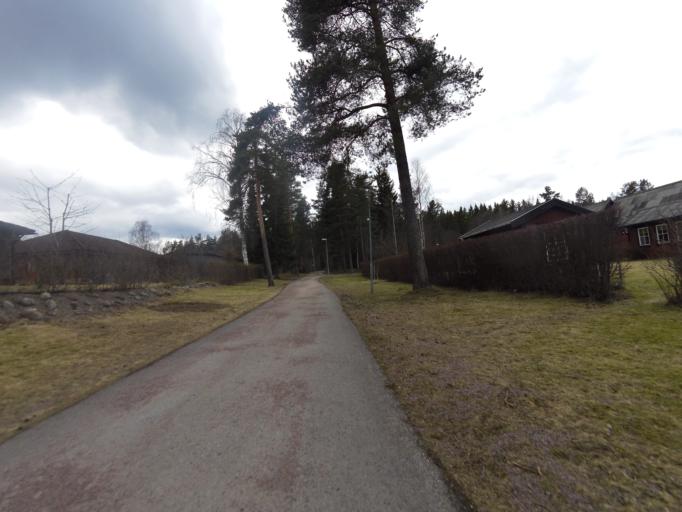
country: SE
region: Gaevleborg
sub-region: Gavle Kommun
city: Gavle
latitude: 60.6917
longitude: 17.0961
